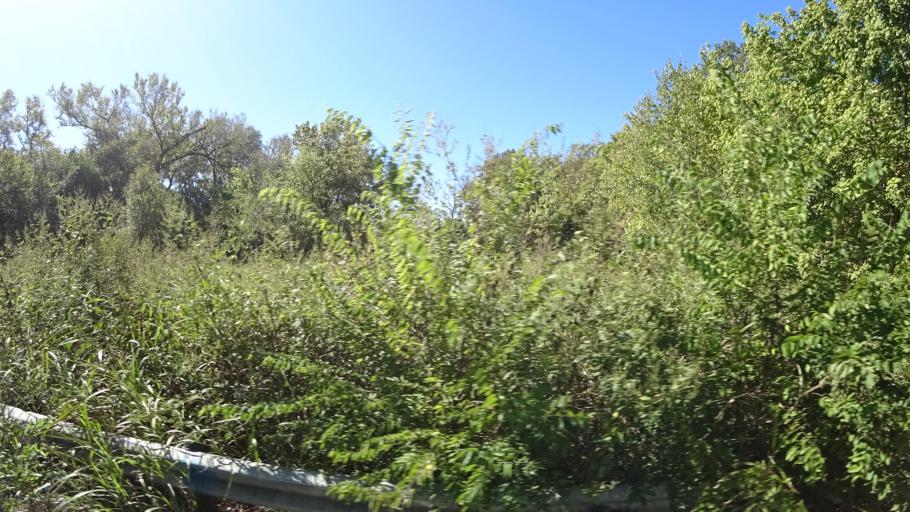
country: US
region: Texas
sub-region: Travis County
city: Hornsby Bend
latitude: 30.2853
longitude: -97.6533
